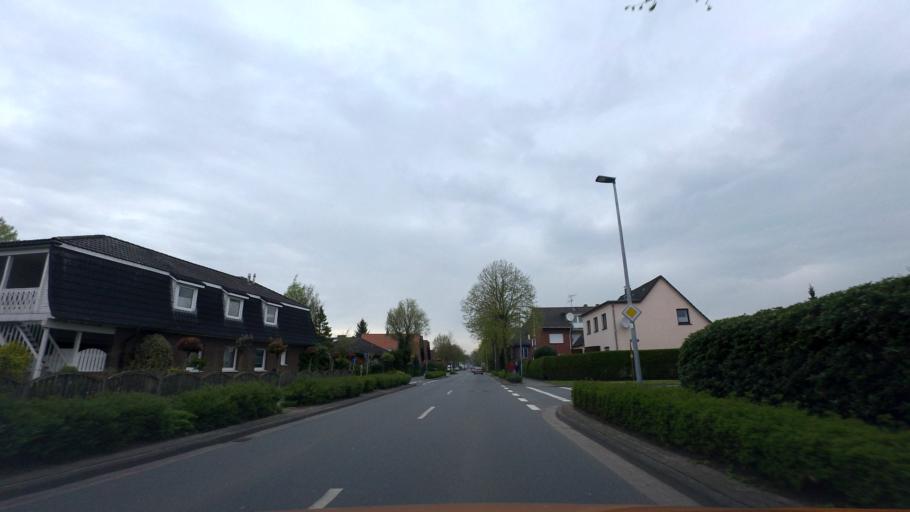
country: DE
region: Lower Saxony
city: Cloppenburg
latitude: 52.8354
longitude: 8.0357
